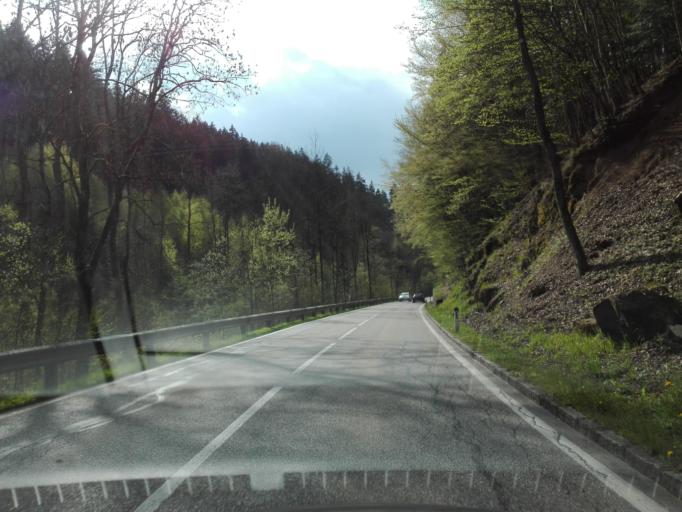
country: AT
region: Upper Austria
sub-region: Politischer Bezirk Urfahr-Umgebung
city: Feldkirchen an der Donau
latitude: 48.3826
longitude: 14.0773
